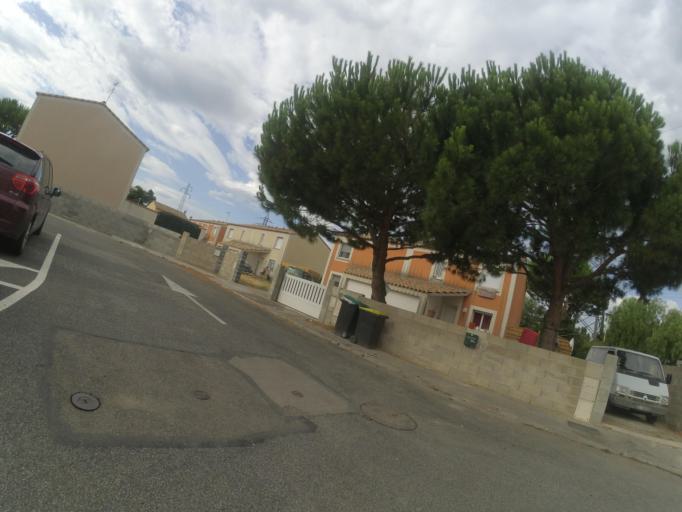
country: FR
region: Languedoc-Roussillon
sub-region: Departement des Pyrenees-Orientales
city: Toulouges
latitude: 42.6764
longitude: 2.8473
